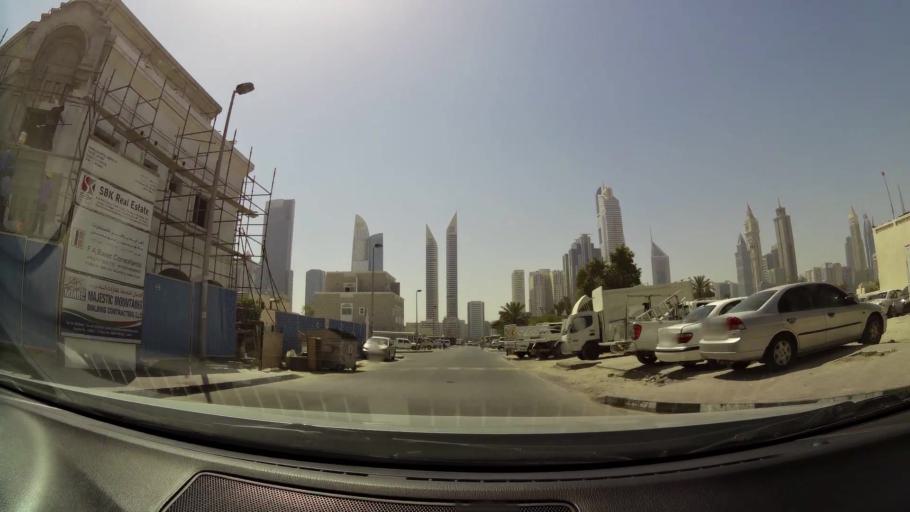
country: AE
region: Ash Shariqah
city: Sharjah
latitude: 25.2270
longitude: 55.2757
